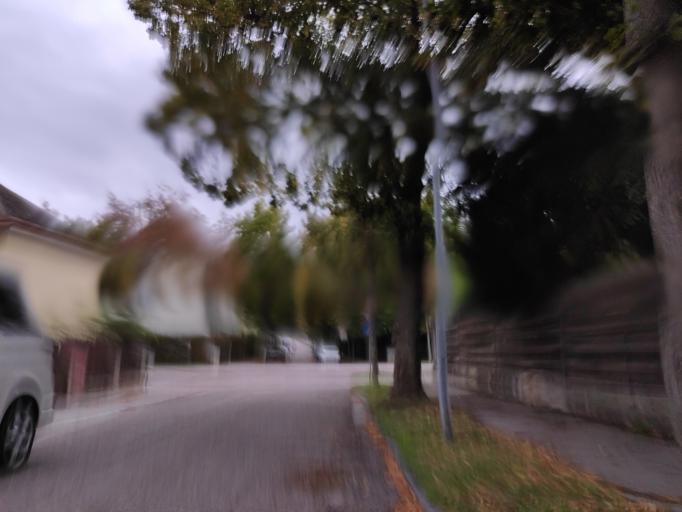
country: AT
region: Lower Austria
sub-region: Politischer Bezirk Baden
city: Pfaffstatten
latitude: 48.0117
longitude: 16.2488
